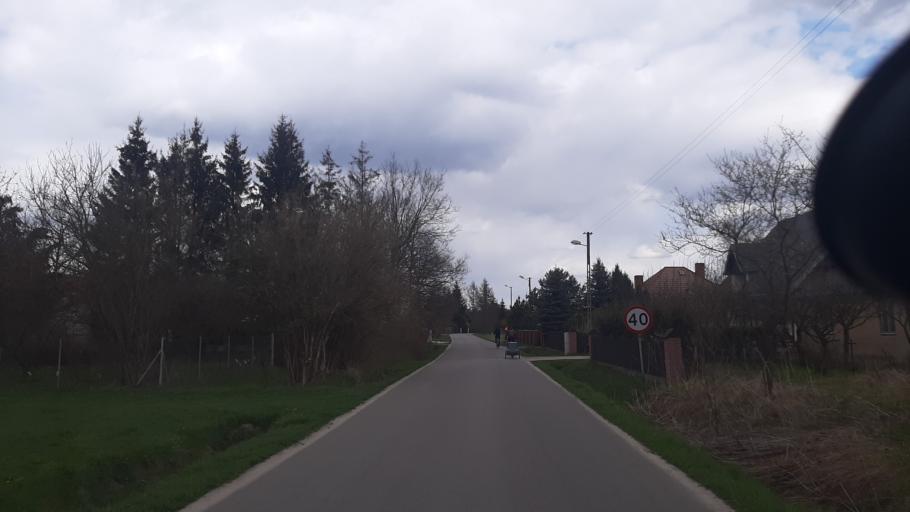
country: PL
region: Lublin Voivodeship
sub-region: Powiat lubelski
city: Niemce
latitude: 51.3818
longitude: 22.5563
